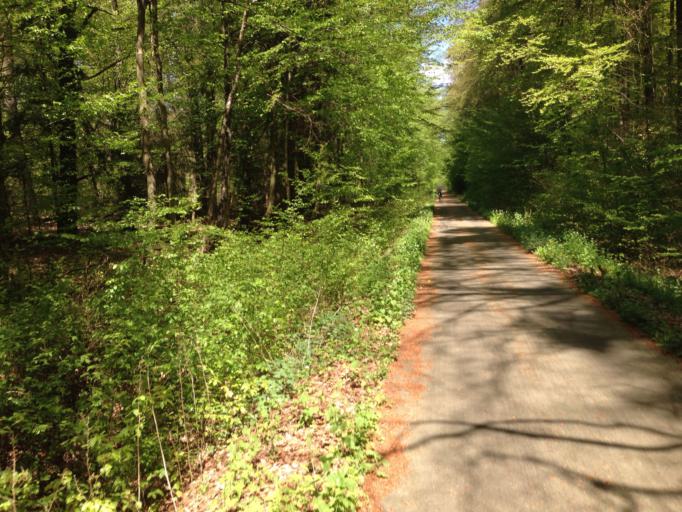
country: DE
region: Hesse
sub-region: Regierungsbezirk Giessen
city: Hungen
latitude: 50.5015
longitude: 8.9107
